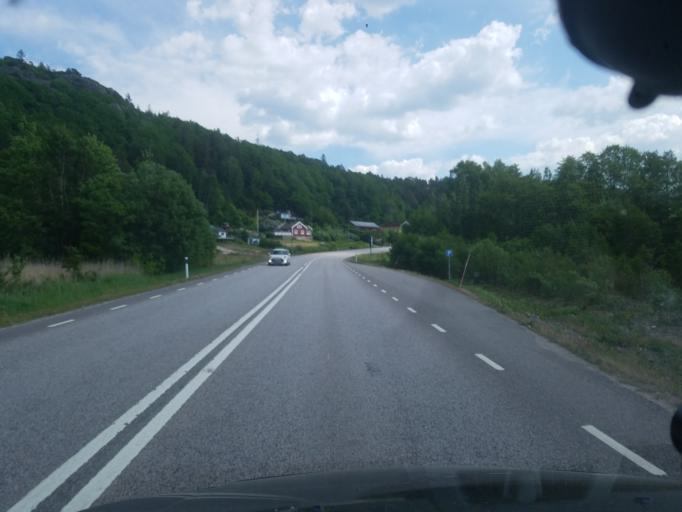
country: SE
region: Vaestra Goetaland
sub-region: Orust
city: Henan
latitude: 58.2507
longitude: 11.6841
